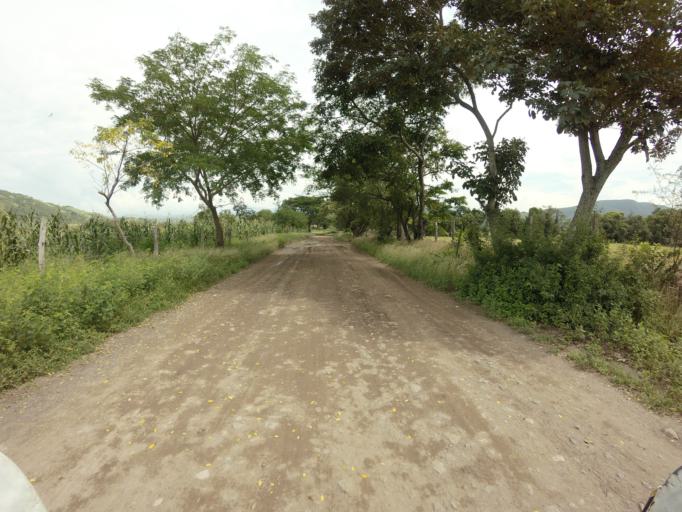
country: CO
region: Tolima
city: Natagaima
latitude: 3.4454
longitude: -75.1401
